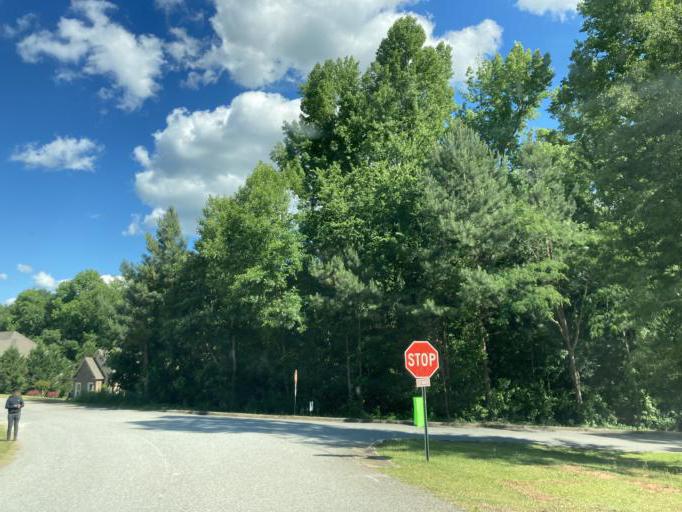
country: US
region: Georgia
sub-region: Jones County
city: Gray
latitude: 32.9949
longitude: -83.5495
